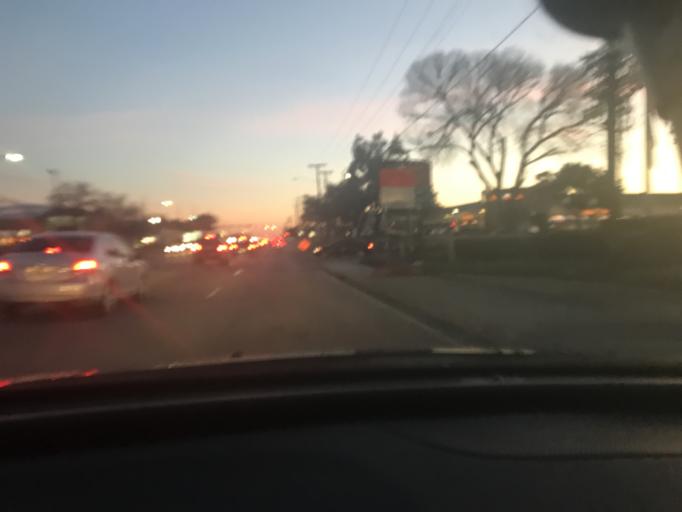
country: US
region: Texas
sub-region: Tarrant County
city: Arlington
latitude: 32.7577
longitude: -97.0974
